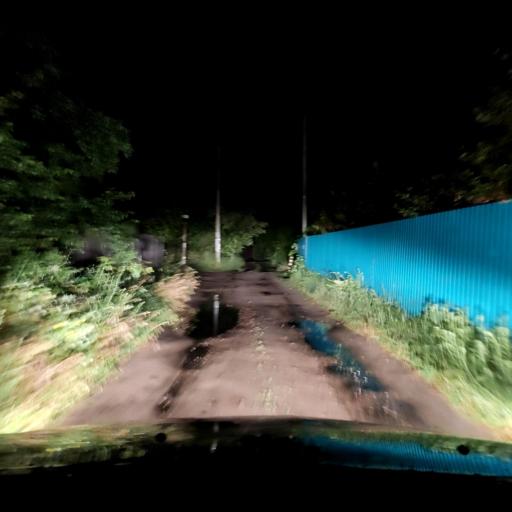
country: RU
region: Voronezj
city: Podkletnoye
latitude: 51.6159
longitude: 39.5178
